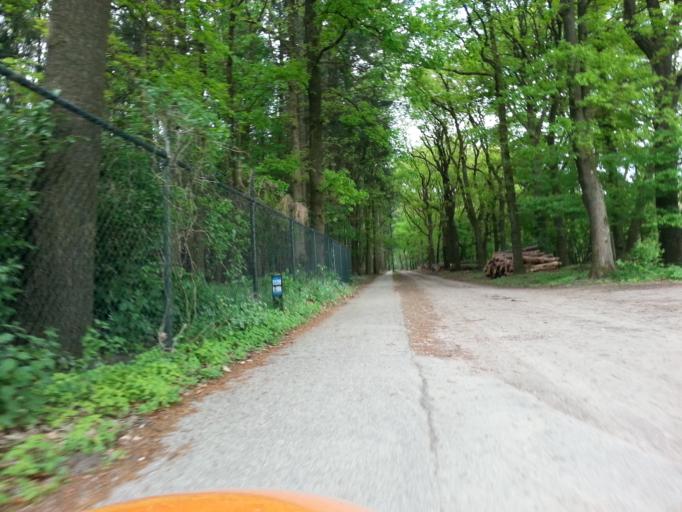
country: NL
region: Gelderland
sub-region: Gemeente Renkum
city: Wolfheze
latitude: 52.0237
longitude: 5.7713
